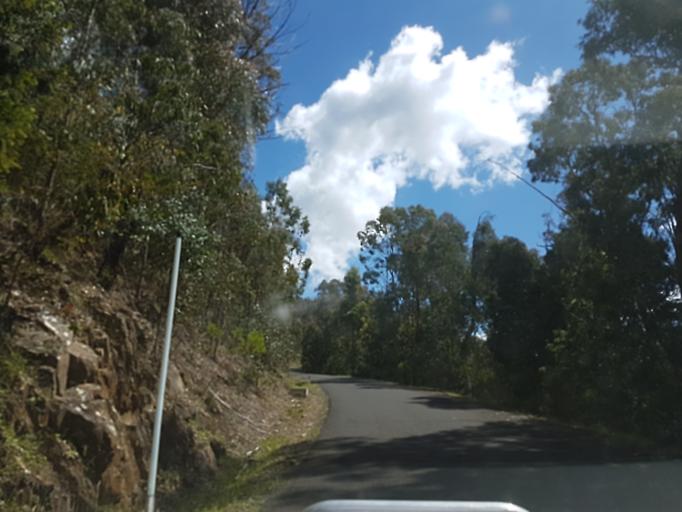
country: AU
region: Victoria
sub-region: East Gippsland
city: Bairnsdale
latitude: -37.4010
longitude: 147.2459
